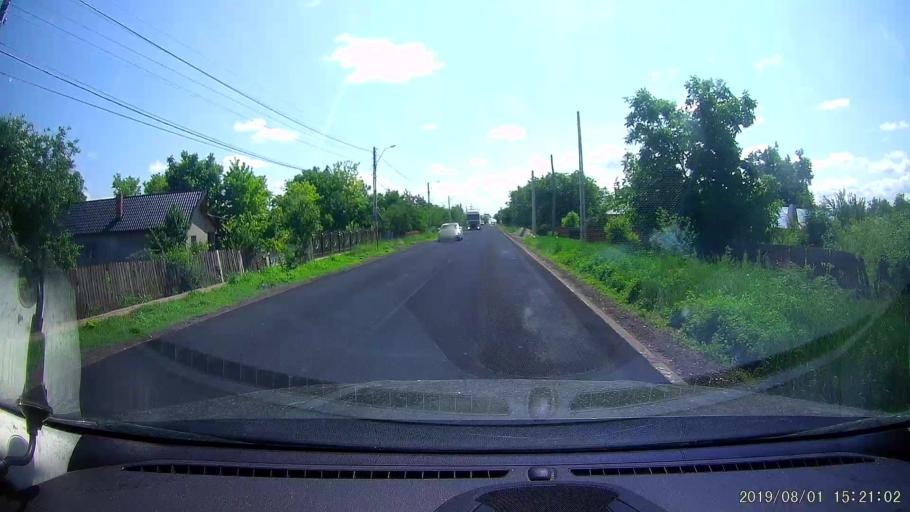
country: RO
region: Braila
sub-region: Comuna Tufesti
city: Tufesti
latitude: 45.0743
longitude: 27.8013
